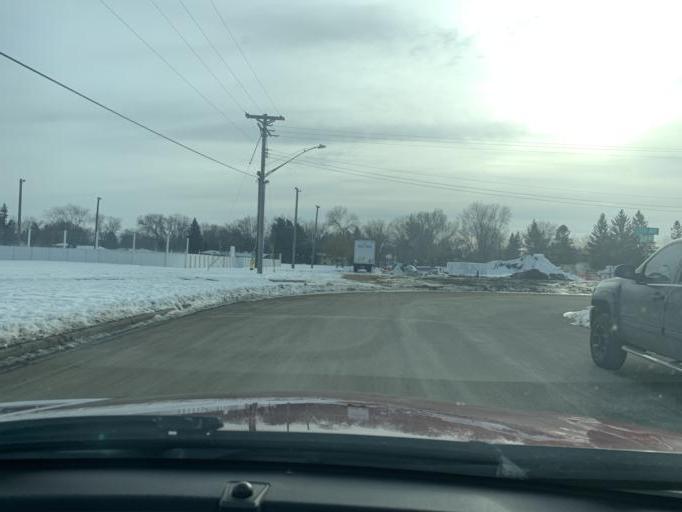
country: US
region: Minnesota
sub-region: Washington County
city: Saint Paul Park
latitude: 44.8350
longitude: -92.9827
